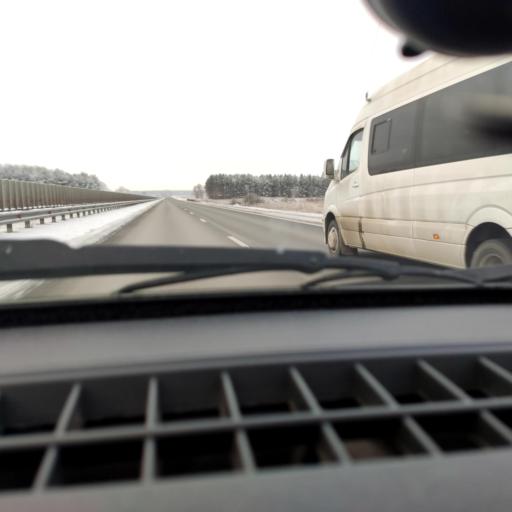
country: RU
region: Bashkortostan
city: Kushnarenkovo
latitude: 55.0603
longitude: 55.4118
